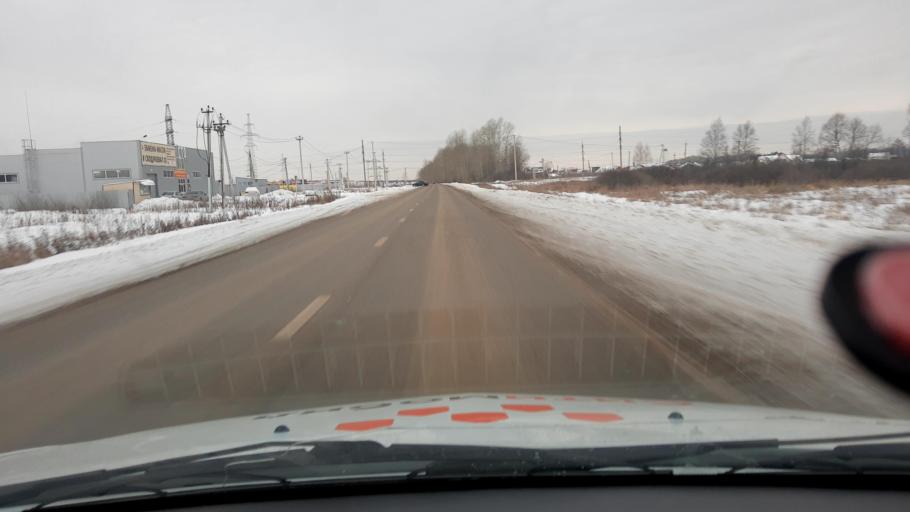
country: RU
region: Bashkortostan
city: Kabakovo
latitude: 54.6805
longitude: 56.1114
